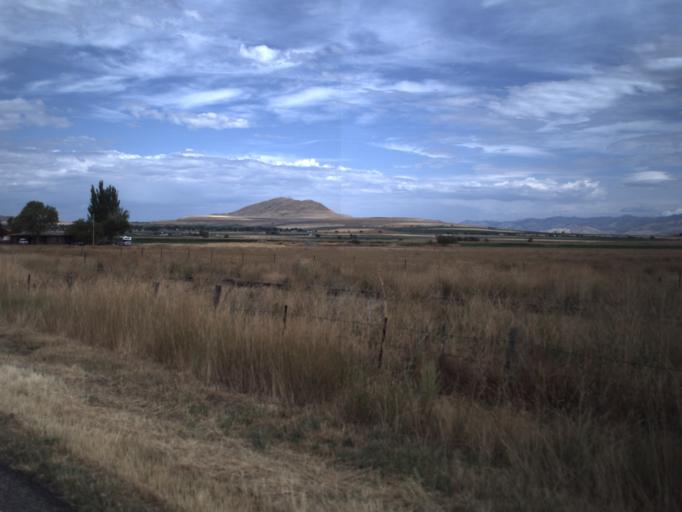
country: US
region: Utah
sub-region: Cache County
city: Benson
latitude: 41.8209
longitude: -111.9984
